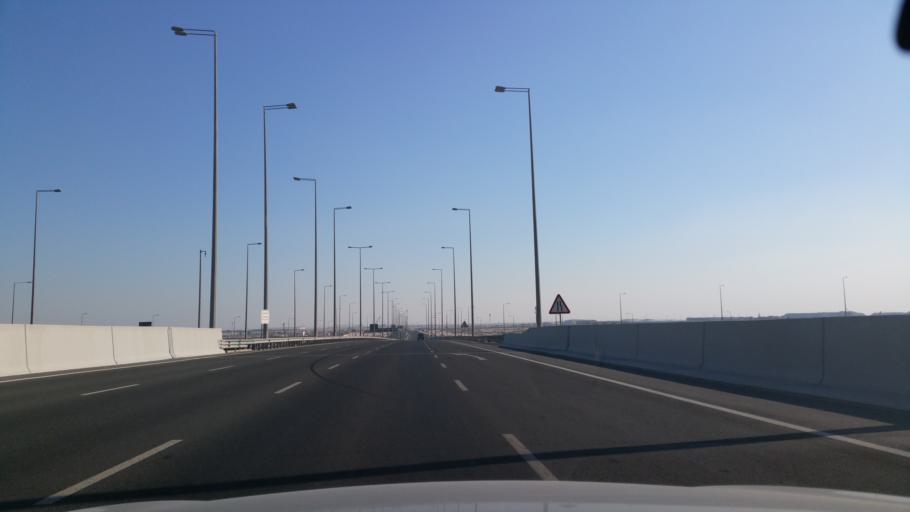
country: QA
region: Al Wakrah
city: Al Wukayr
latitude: 25.1653
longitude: 51.4722
